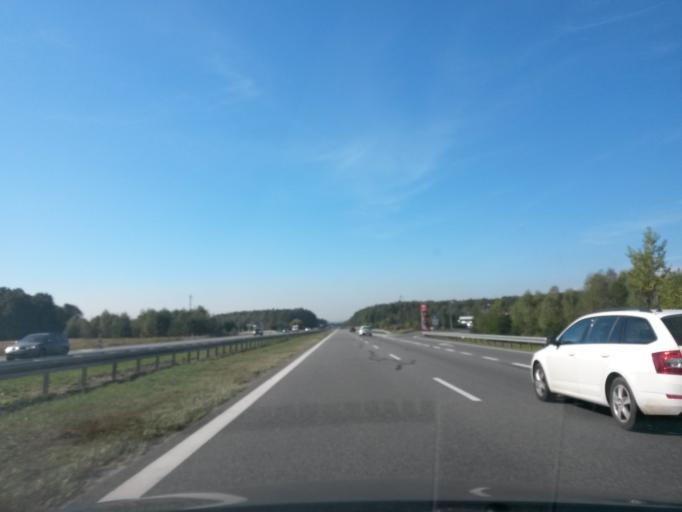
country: PL
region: Lesser Poland Voivodeship
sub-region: Powiat chrzanowski
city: Libiaz
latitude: 50.1481
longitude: 19.3039
